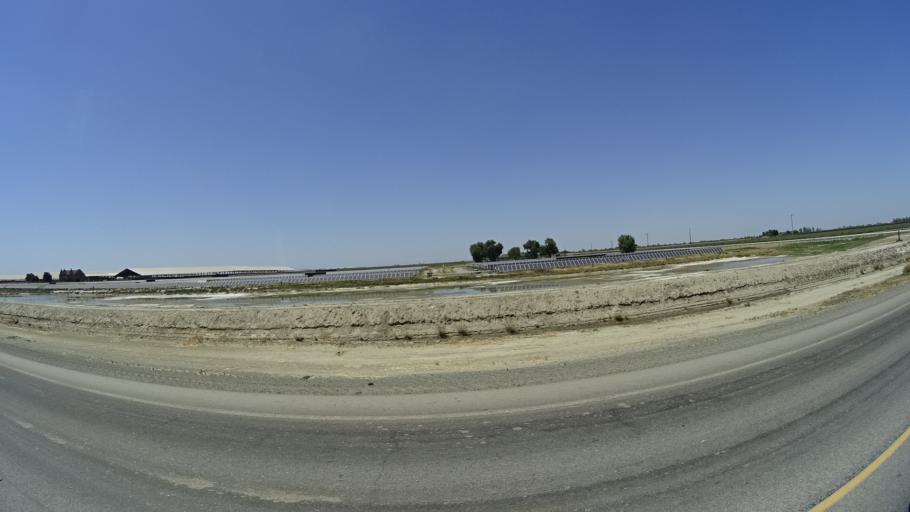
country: US
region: California
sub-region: Kings County
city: Home Garden
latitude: 36.1955
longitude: -119.6459
